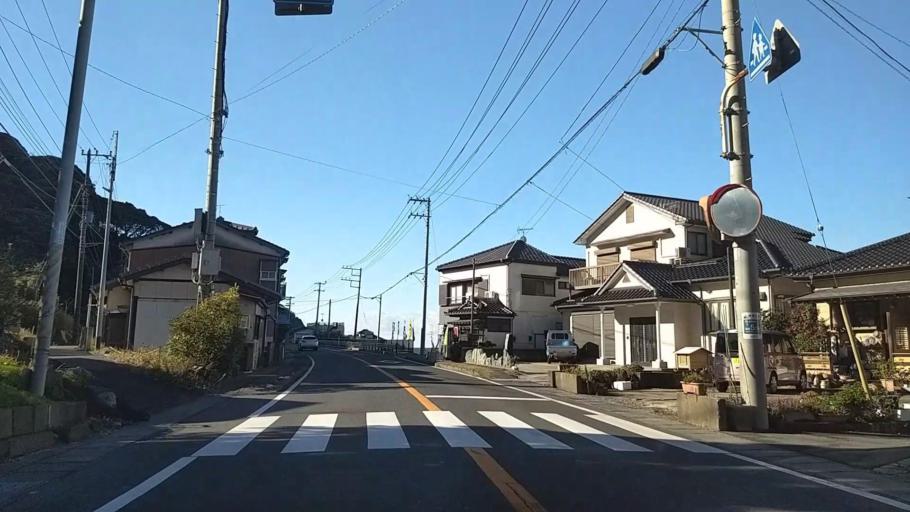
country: JP
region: Chiba
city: Futtsu
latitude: 35.1967
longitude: 139.8249
